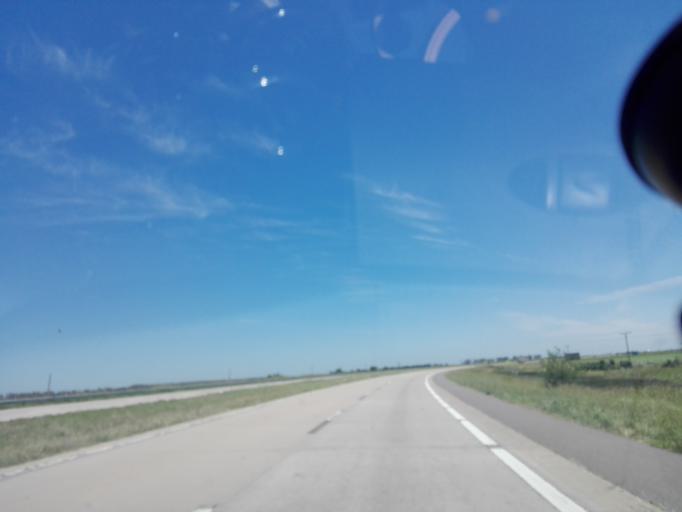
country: AR
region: Cordoba
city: General Roca
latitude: -32.7036
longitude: -61.9444
